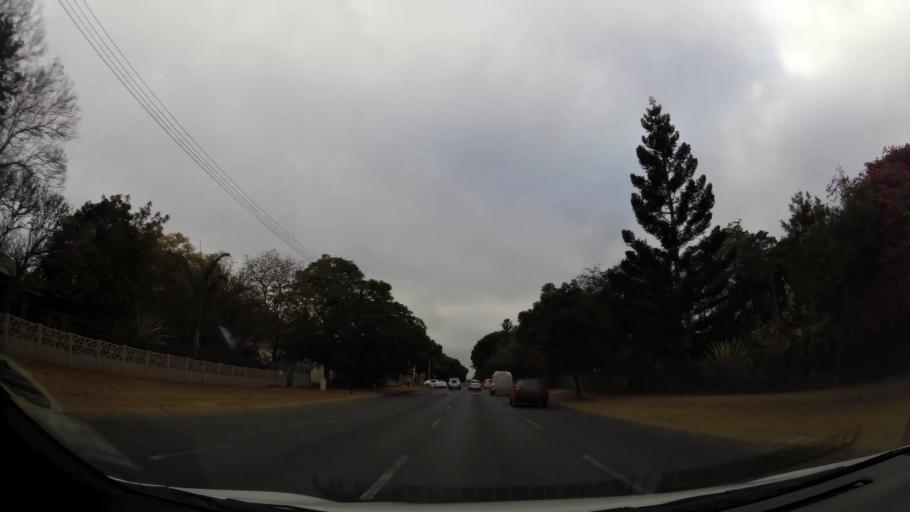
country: ZA
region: Limpopo
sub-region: Capricorn District Municipality
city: Polokwane
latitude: -23.9000
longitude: 29.4641
